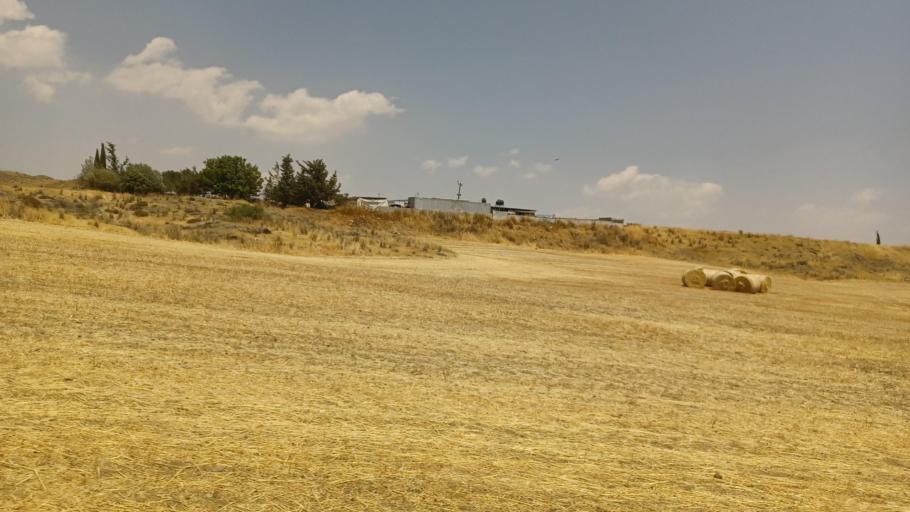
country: CY
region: Larnaka
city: Troulloi
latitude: 35.0163
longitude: 33.6048
